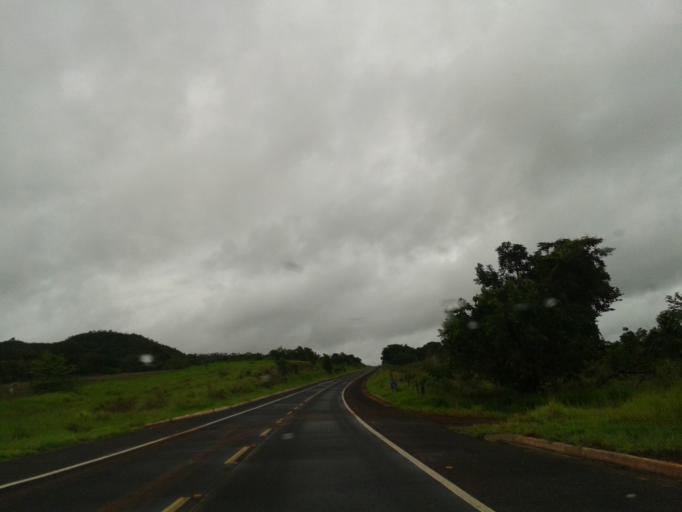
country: BR
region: Minas Gerais
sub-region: Santa Vitoria
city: Santa Vitoria
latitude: -19.1983
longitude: -50.0299
